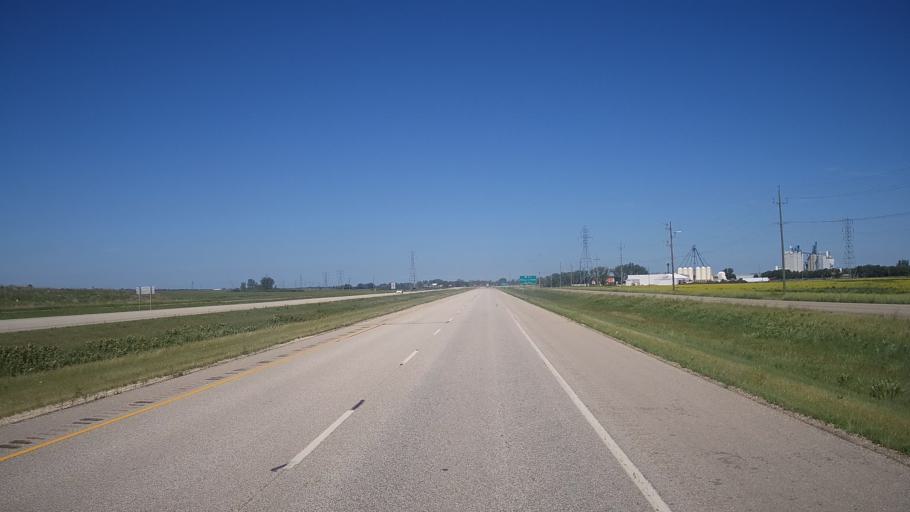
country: CA
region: Manitoba
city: Portage la Prairie
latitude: 49.9582
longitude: -98.3383
